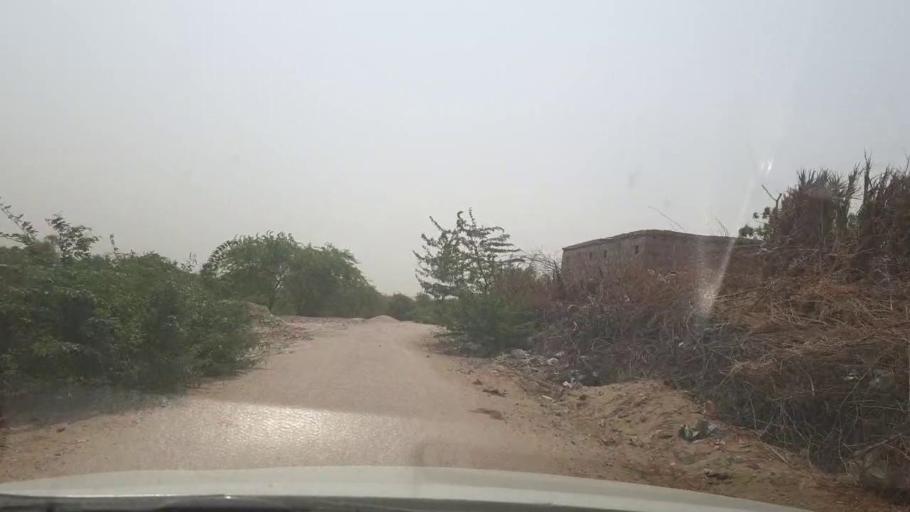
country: PK
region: Sindh
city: Kot Diji
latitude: 27.3379
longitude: 68.7124
